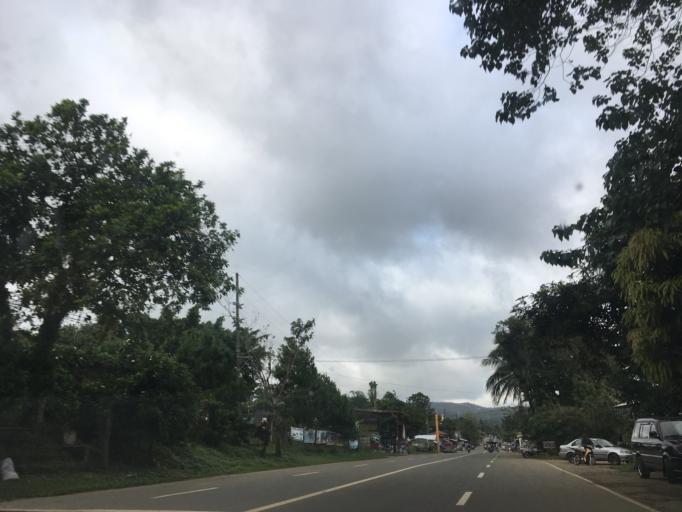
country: PH
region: Calabarzon
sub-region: Province of Rizal
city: Sampaloc
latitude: 14.5343
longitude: 121.3621
